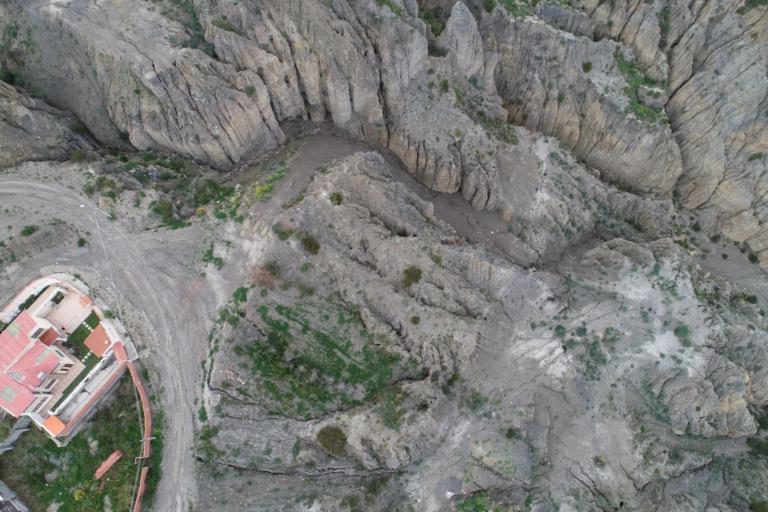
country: BO
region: La Paz
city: La Paz
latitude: -16.4984
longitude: -68.0801
